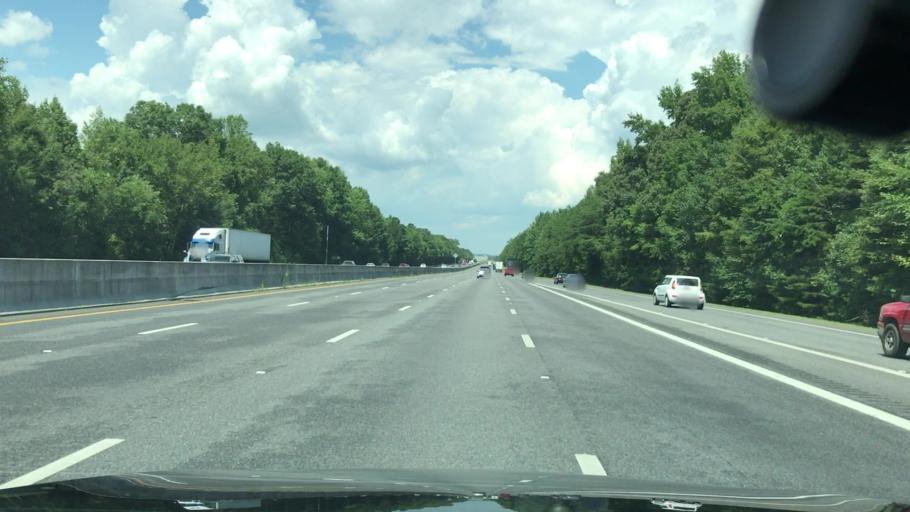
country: US
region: South Carolina
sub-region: York County
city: Lesslie
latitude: 34.9166
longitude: -80.9806
